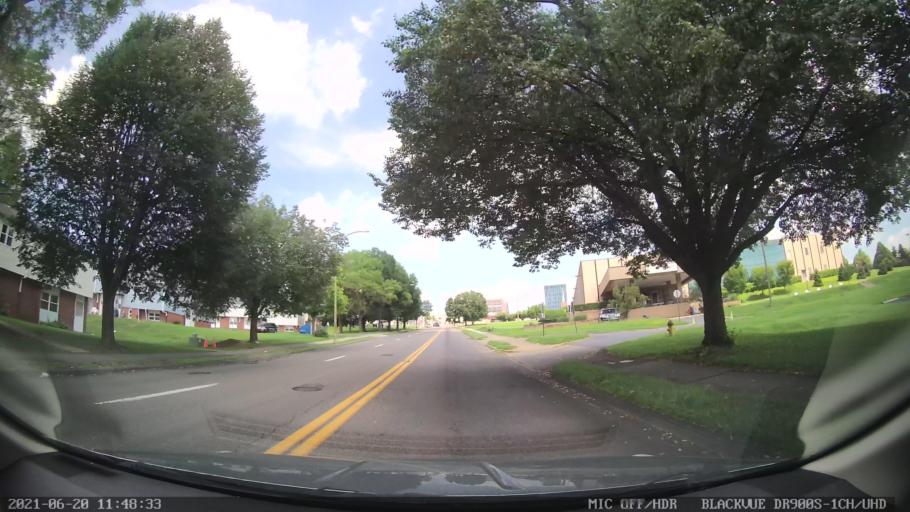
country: US
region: Pennsylvania
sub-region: Lehigh County
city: Allentown
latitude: 40.5983
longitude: -75.4679
